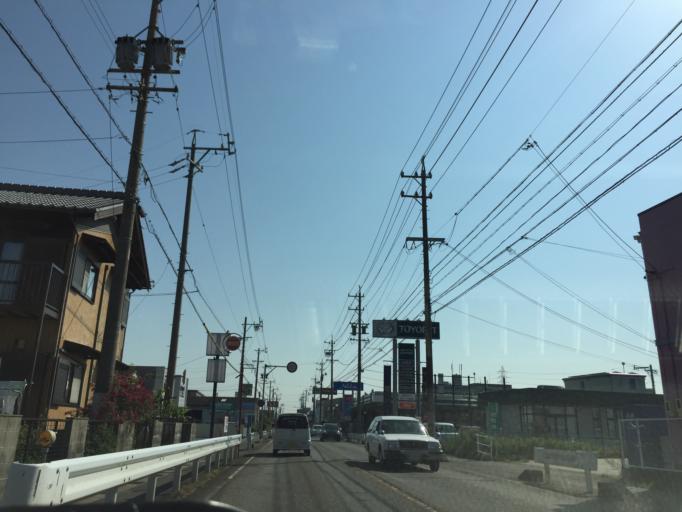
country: JP
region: Mie
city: Yokkaichi
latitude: 34.9879
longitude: 136.6369
